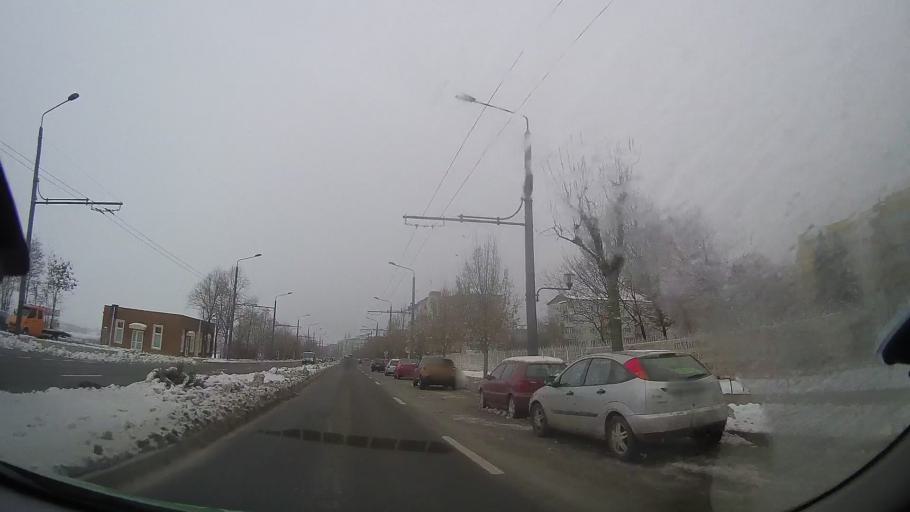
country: RO
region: Vaslui
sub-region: Municipiul Vaslui
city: Moara Grecilor
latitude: 46.6535
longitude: 27.7375
